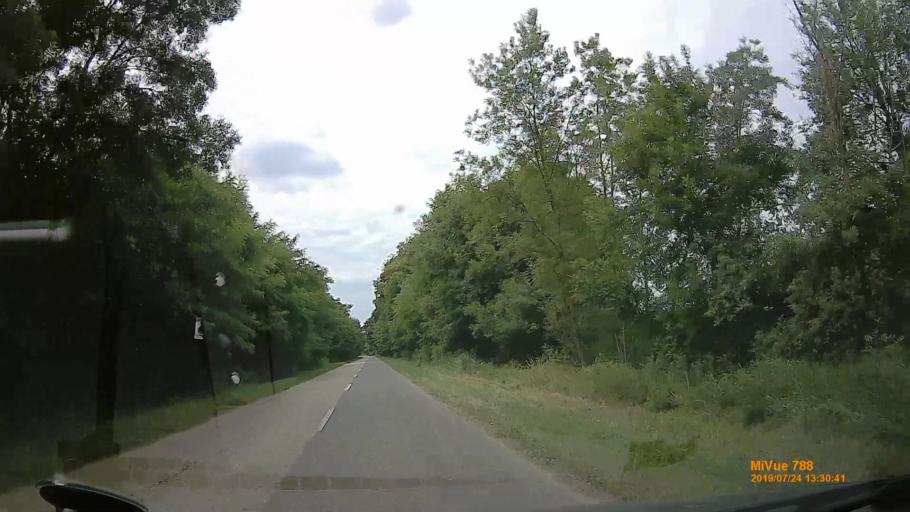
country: HU
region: Szabolcs-Szatmar-Bereg
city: Aranyosapati
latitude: 48.2316
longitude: 22.3745
